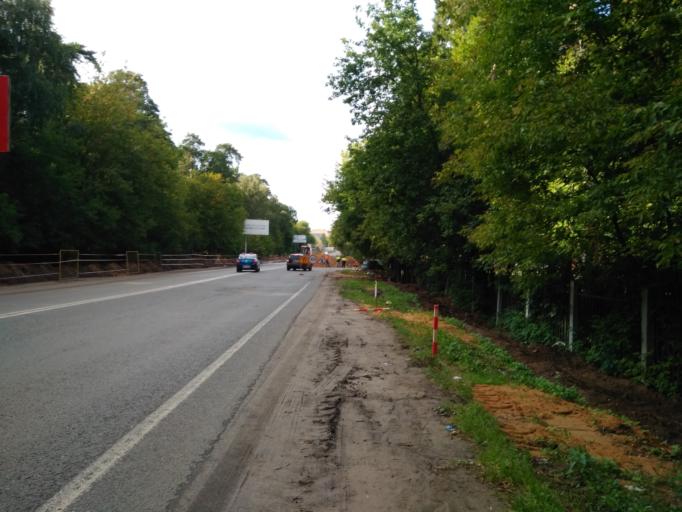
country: RU
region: Moskovskaya
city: Zhukovskiy
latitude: 55.5858
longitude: 38.1217
